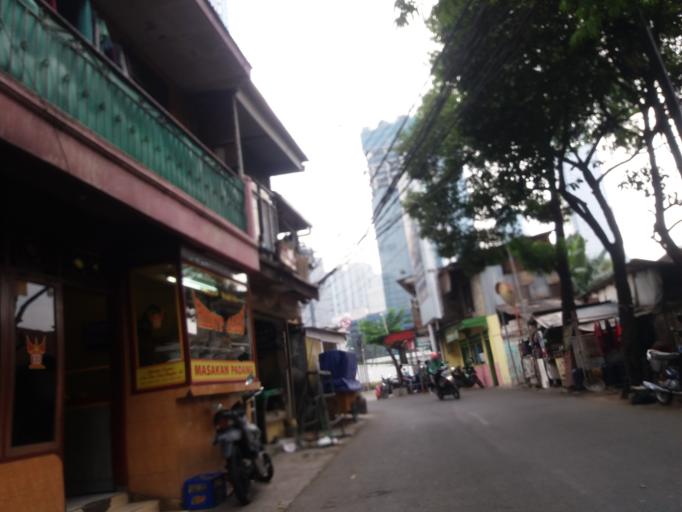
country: ID
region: Jakarta Raya
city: Jakarta
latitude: -6.2161
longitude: 106.8221
